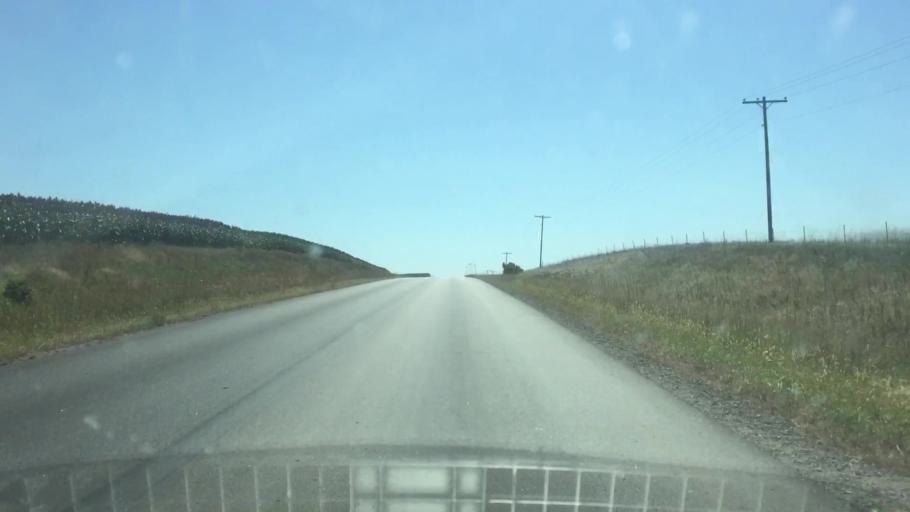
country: US
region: Kansas
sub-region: Marshall County
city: Marysville
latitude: 39.8985
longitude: -96.6012
